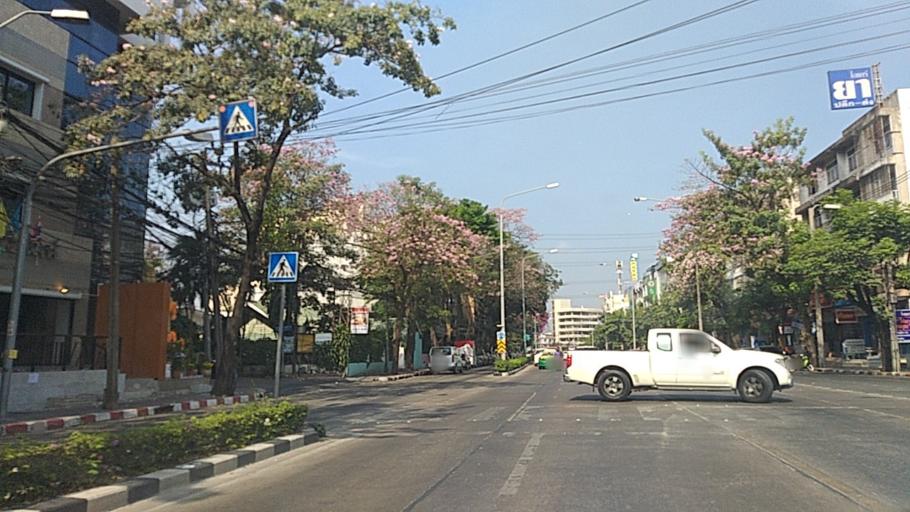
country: TH
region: Bangkok
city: Chatuchak
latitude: 13.8402
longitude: 100.5447
